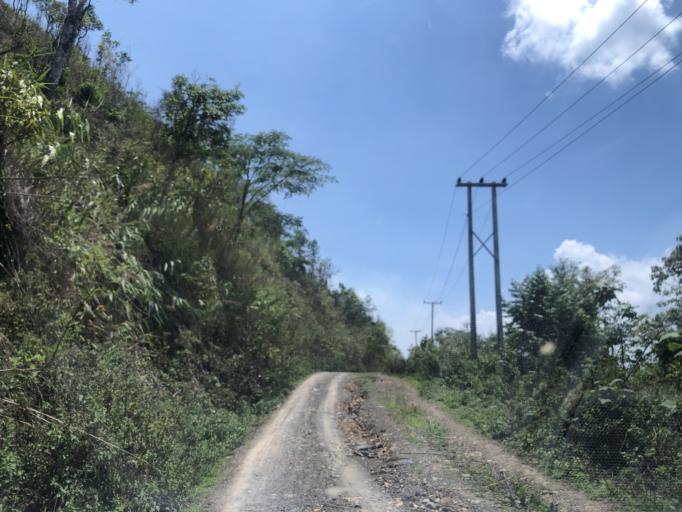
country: LA
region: Phongsali
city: Phongsali
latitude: 21.4375
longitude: 102.1620
